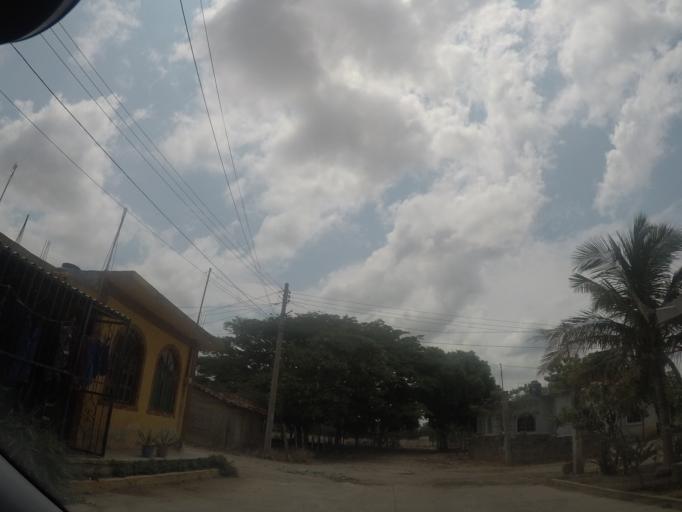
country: MX
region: Oaxaca
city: El Espinal
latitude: 16.5552
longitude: -94.9429
